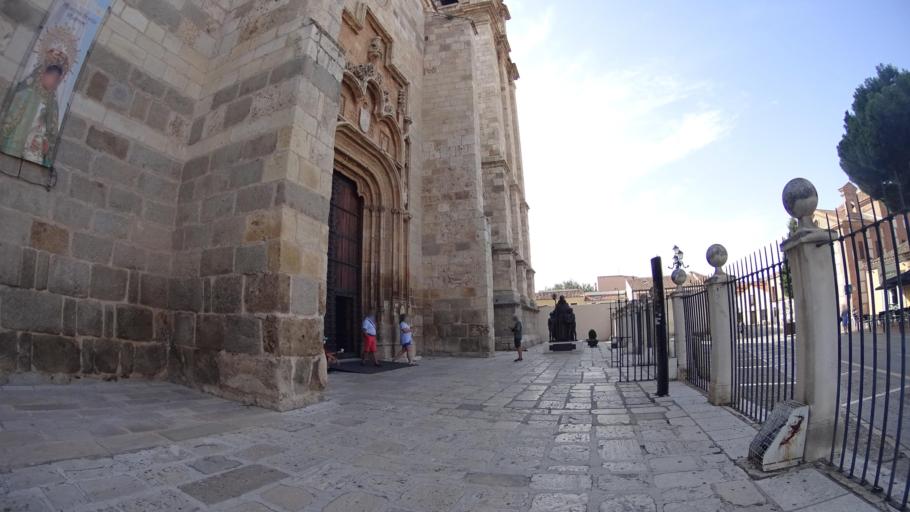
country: ES
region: Madrid
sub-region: Provincia de Madrid
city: Alcala de Henares
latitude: 40.4805
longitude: -3.3694
